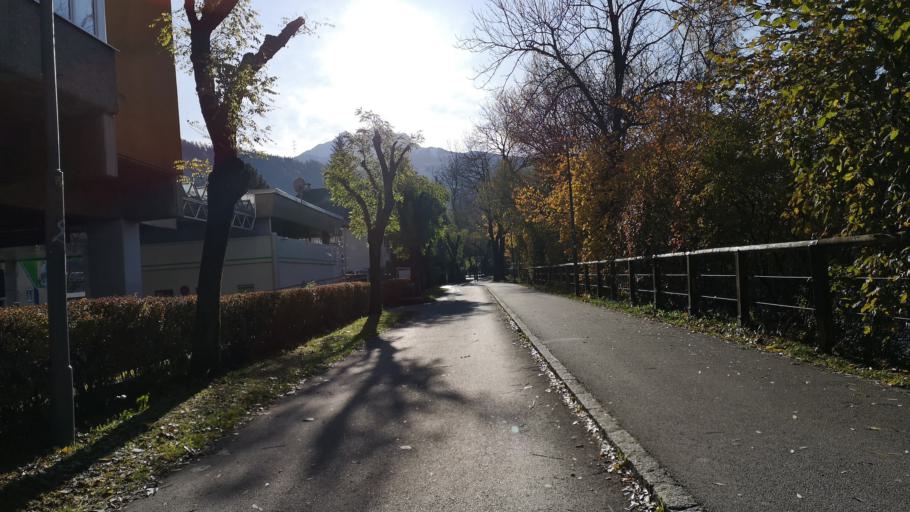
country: AT
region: Tyrol
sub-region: Innsbruck Stadt
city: Innsbruck
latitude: 47.2578
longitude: 11.3784
